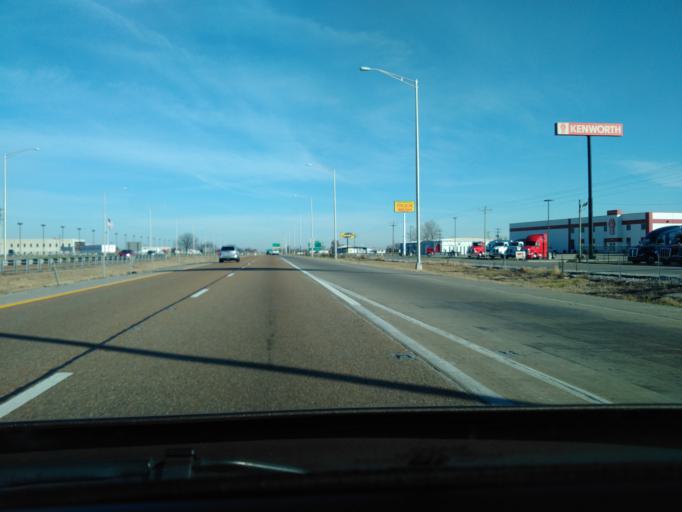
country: US
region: Illinois
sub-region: Madison County
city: Troy
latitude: 38.7365
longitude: -89.9113
